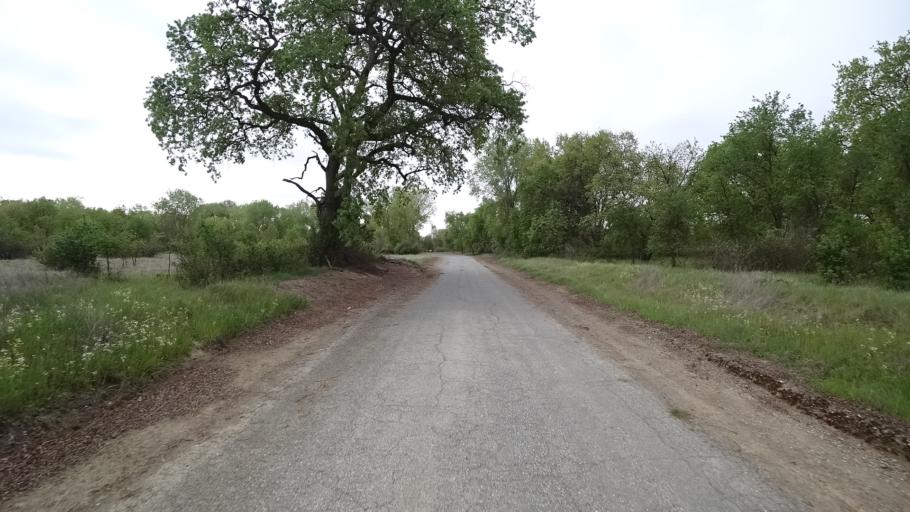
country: US
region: California
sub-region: Colusa County
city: Colusa
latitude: 39.4103
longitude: -122.0067
